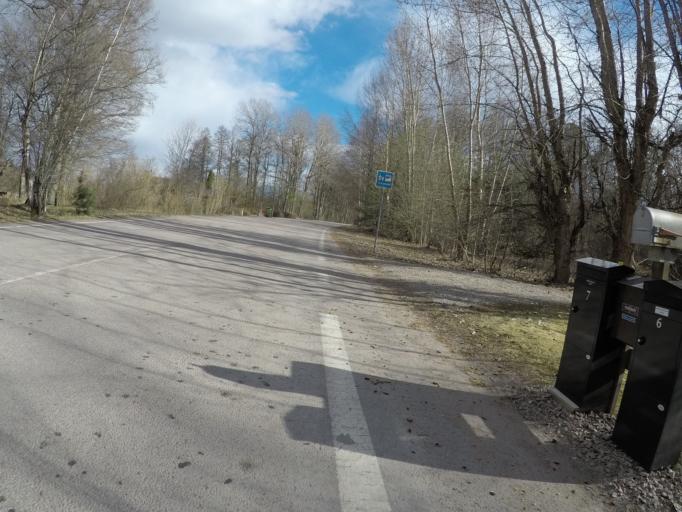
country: SE
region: Soedermanland
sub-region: Eskilstuna Kommun
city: Kvicksund
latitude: 59.4800
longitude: 16.2849
